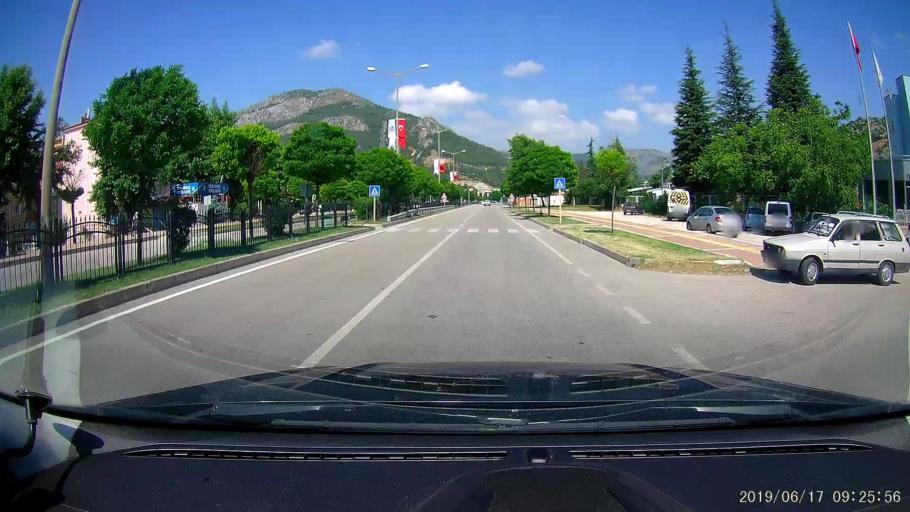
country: TR
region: Amasya
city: Amasya
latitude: 40.6684
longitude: 35.8423
